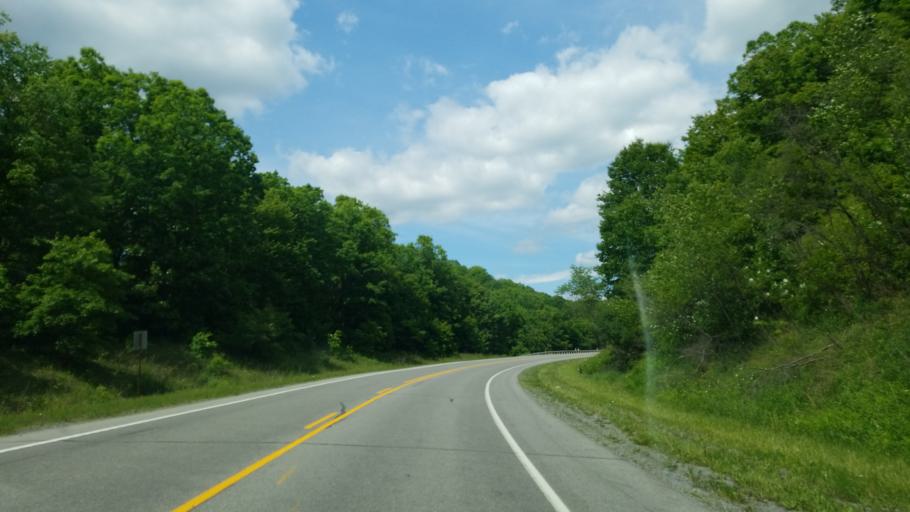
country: US
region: Pennsylvania
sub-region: Clearfield County
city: Clearfield
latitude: 40.9556
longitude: -78.3736
